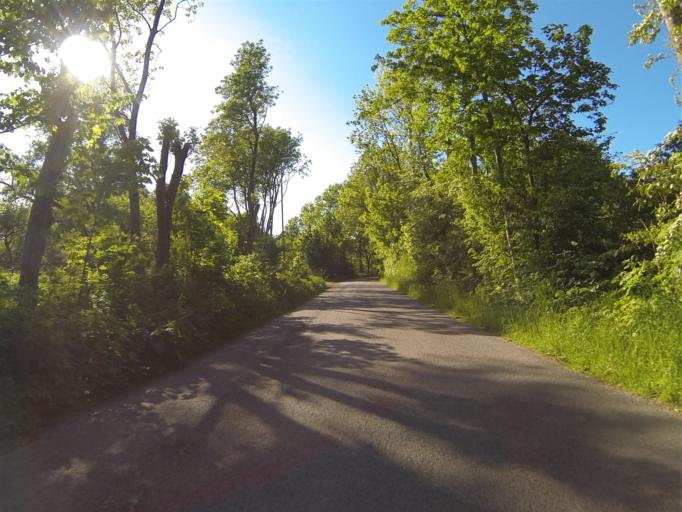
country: SE
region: Skane
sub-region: Lunds Kommun
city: Genarp
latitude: 55.6796
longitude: 13.4047
